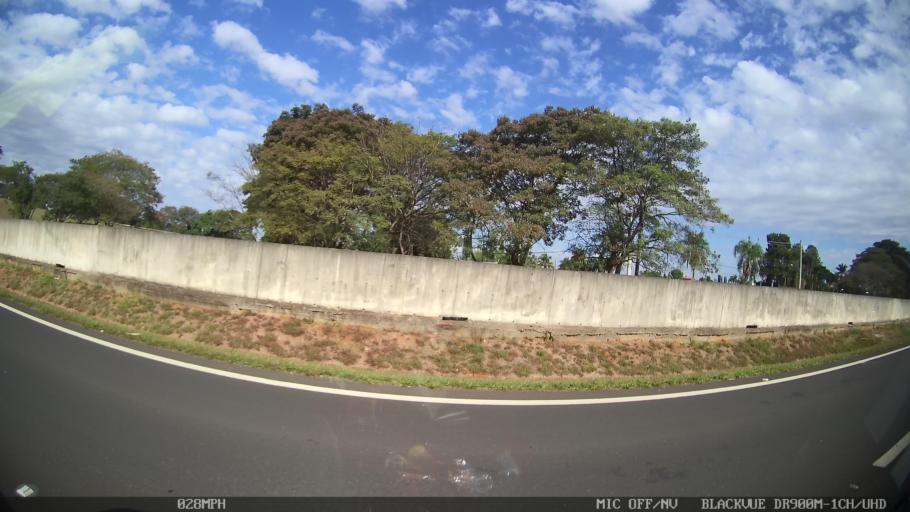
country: BR
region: Sao Paulo
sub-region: Limeira
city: Limeira
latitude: -22.5674
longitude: -47.4389
